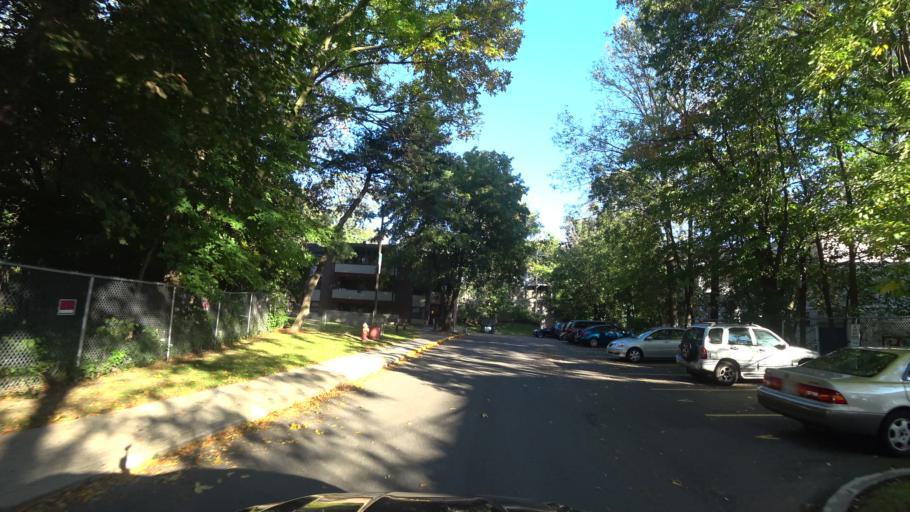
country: US
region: Massachusetts
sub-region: Suffolk County
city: Jamaica Plain
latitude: 42.3075
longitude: -71.1049
